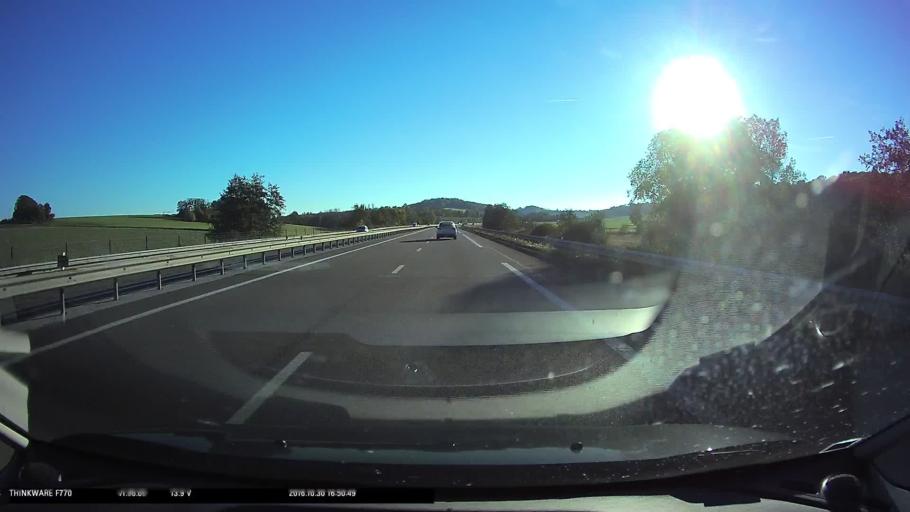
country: FR
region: Franche-Comte
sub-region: Departement du Doubs
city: Pelousey
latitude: 47.2644
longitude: 5.9228
